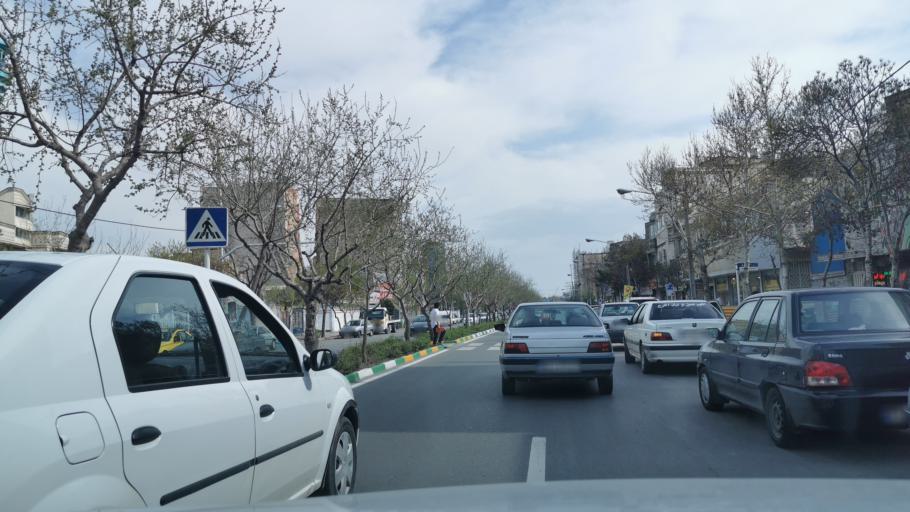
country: IR
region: Razavi Khorasan
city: Mashhad
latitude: 36.3141
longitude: 59.6117
